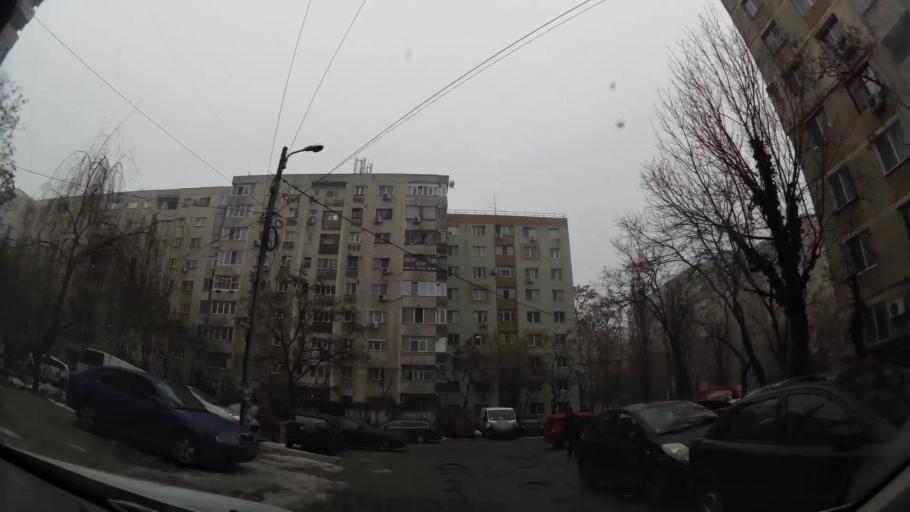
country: RO
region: Ilfov
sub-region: Comuna Chiajna
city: Rosu
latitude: 44.4577
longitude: 26.0490
